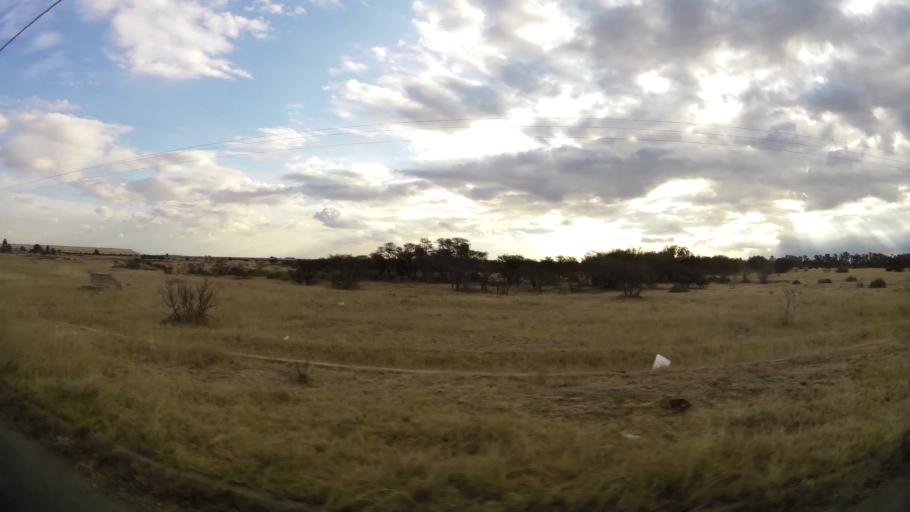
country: ZA
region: Orange Free State
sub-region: Lejweleputswa District Municipality
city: Welkom
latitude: -28.0061
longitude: 26.7100
